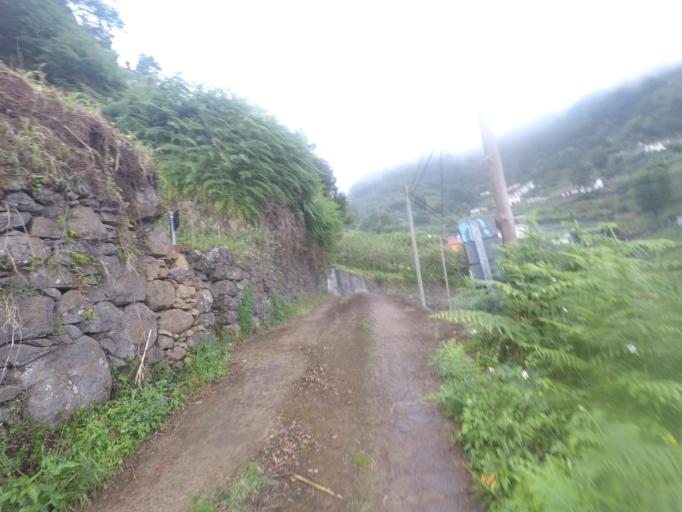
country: PT
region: Madeira
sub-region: Santana
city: Santana
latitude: 32.7707
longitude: -16.8774
